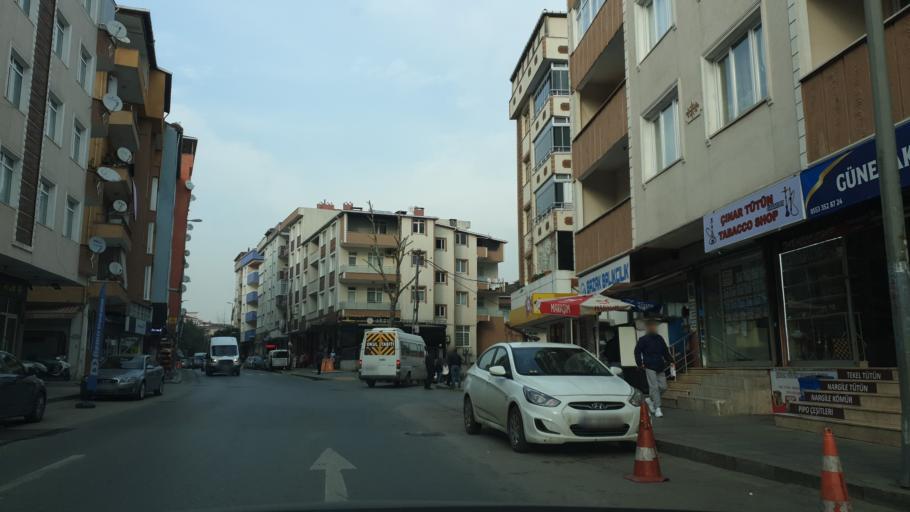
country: TR
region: Istanbul
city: Pendik
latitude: 40.8762
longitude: 29.2732
